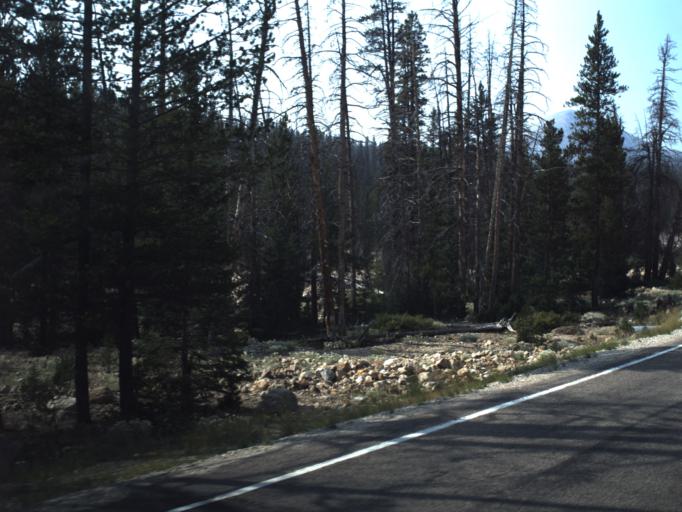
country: US
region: Utah
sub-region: Summit County
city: Kamas
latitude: 40.6738
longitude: -110.9515
